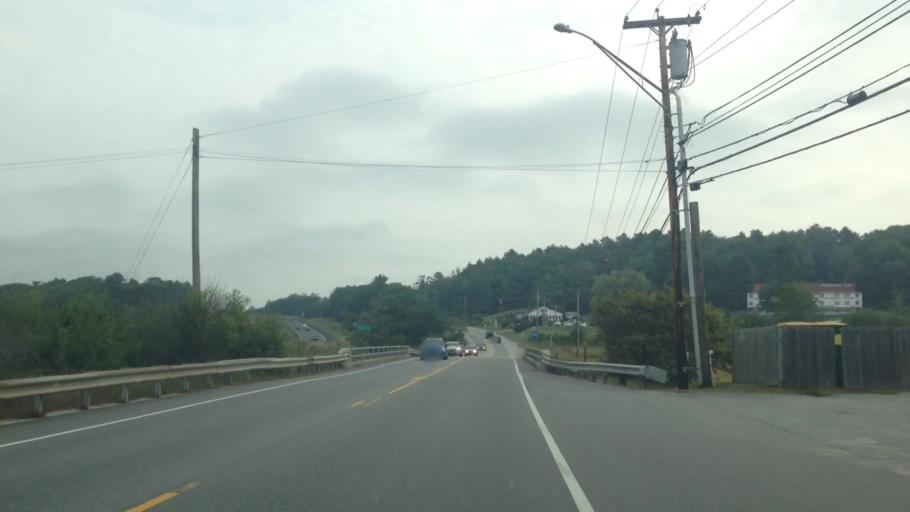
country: US
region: Maine
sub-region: Cumberland County
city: Yarmouth
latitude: 43.8125
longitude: -70.1540
